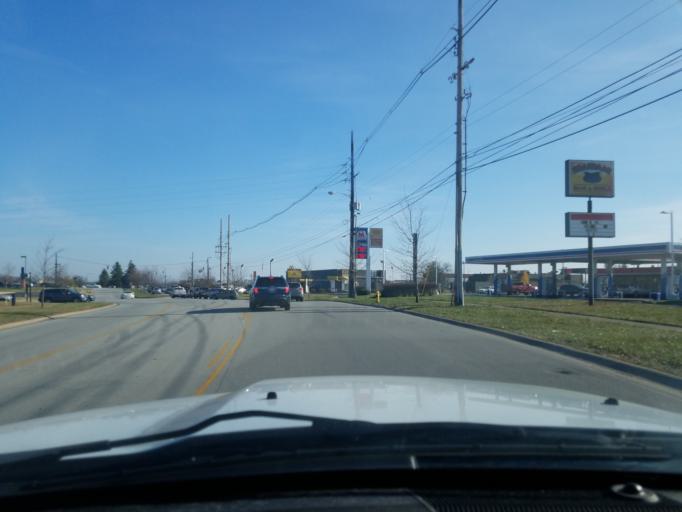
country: US
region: Kentucky
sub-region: Jefferson County
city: Douglass Hills
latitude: 38.2168
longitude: -85.5409
